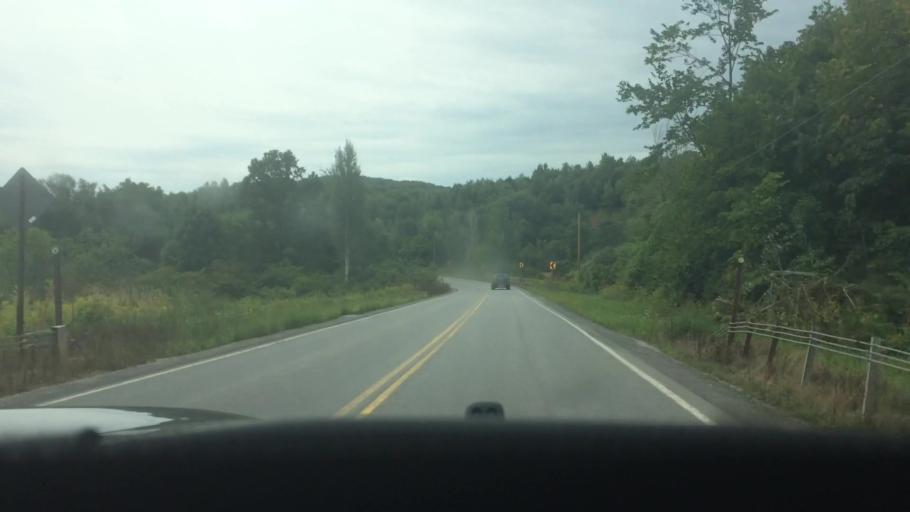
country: US
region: New York
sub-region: St. Lawrence County
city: Canton
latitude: 44.4863
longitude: -75.2486
